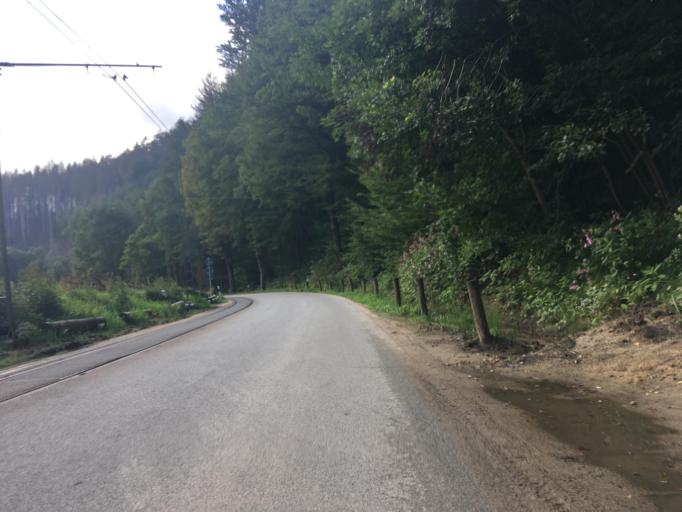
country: DE
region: Saxony
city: Sebnitz
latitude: 50.9266
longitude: 14.2255
